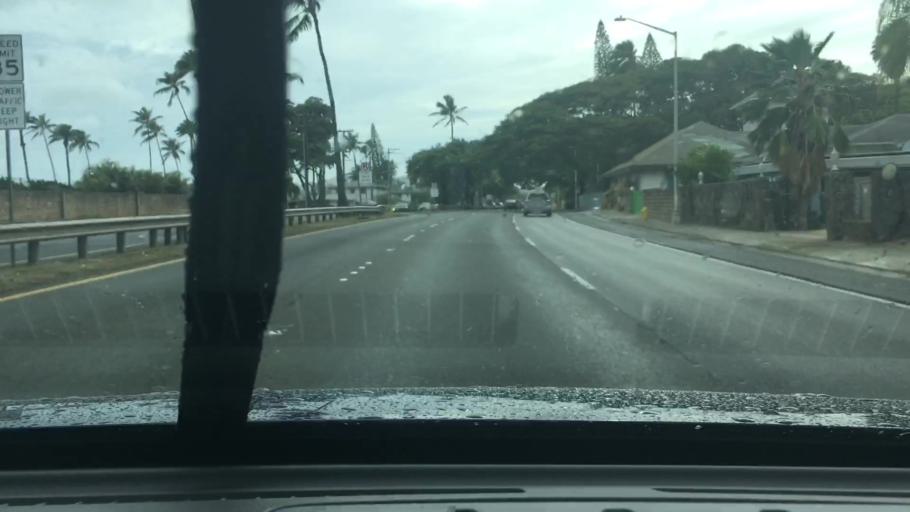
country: US
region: Hawaii
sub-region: Honolulu County
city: Waimanalo
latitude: 21.2770
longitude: -157.7590
